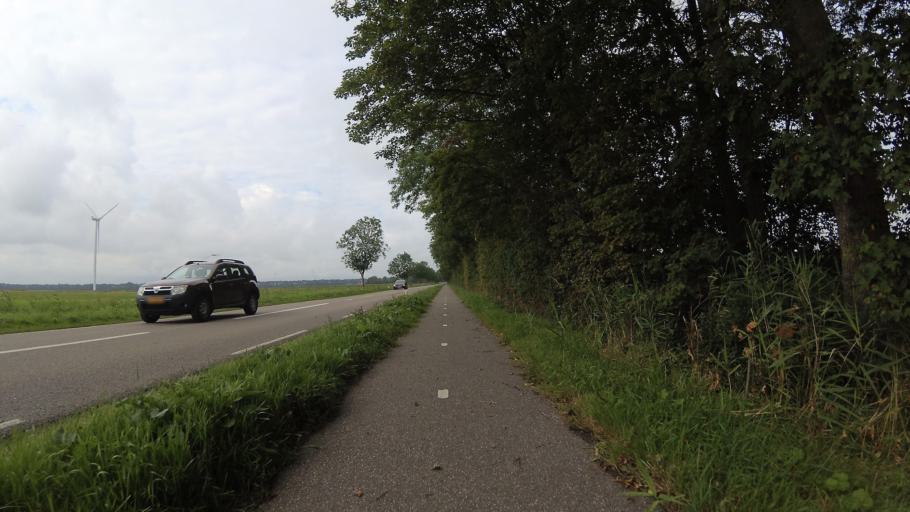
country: NL
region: North Holland
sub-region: Gemeente Schagen
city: Schagen
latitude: 52.8354
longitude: 4.9195
